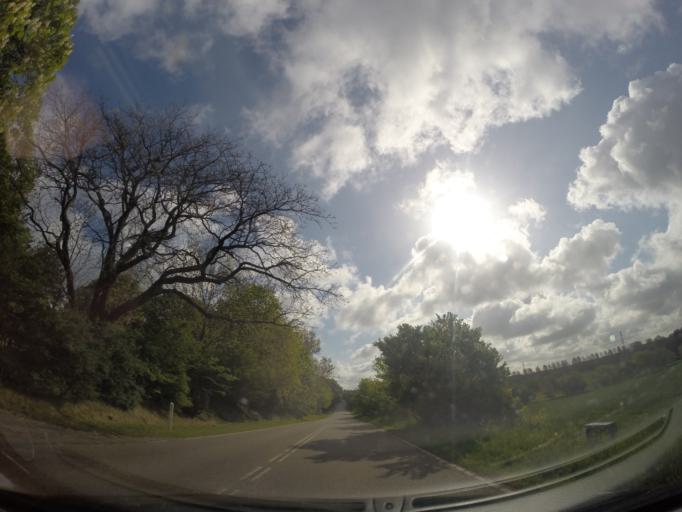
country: DK
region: Capital Region
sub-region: Hoje-Taastrup Kommune
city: Taastrup
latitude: 55.6794
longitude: 12.3101
